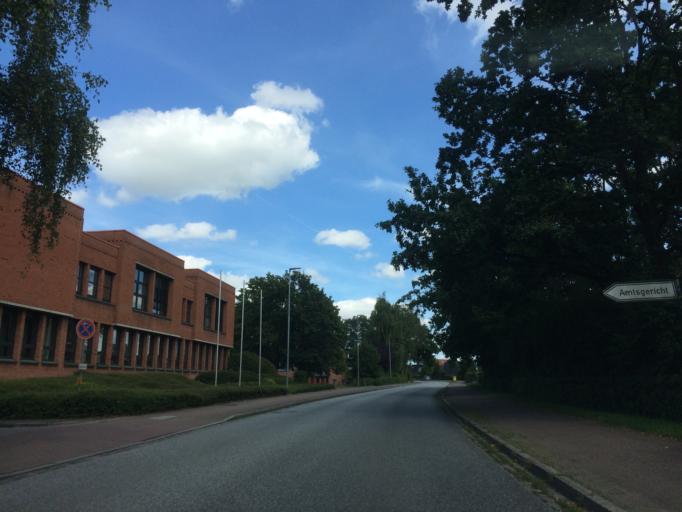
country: DE
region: Schleswig-Holstein
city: Ploen
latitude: 54.1667
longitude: 10.4320
